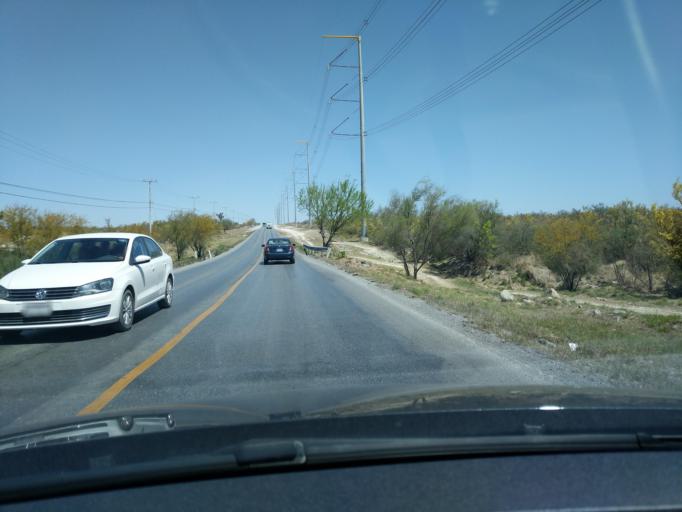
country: MX
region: Nuevo Leon
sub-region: Apodaca
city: Artemio Trevino
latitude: 25.8195
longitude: -100.1451
